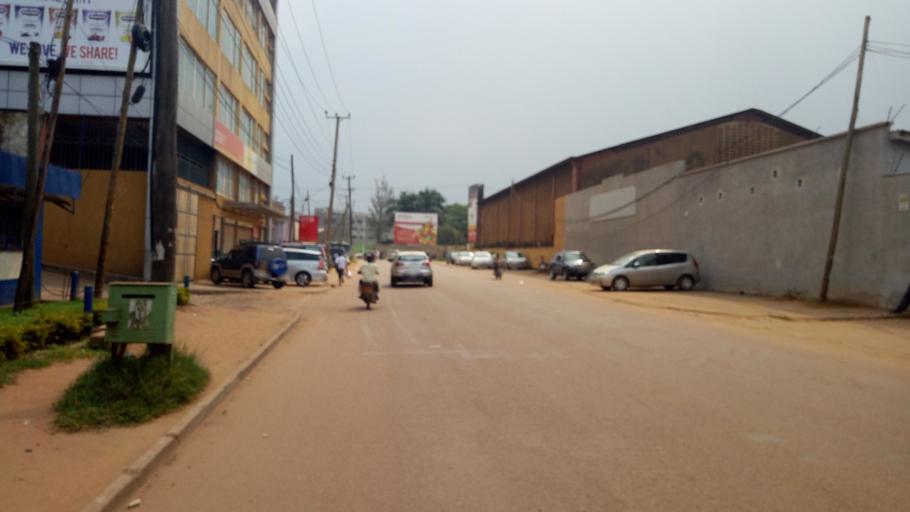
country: UG
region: Central Region
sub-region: Kampala District
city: Kampala
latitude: 0.3143
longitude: 32.6122
